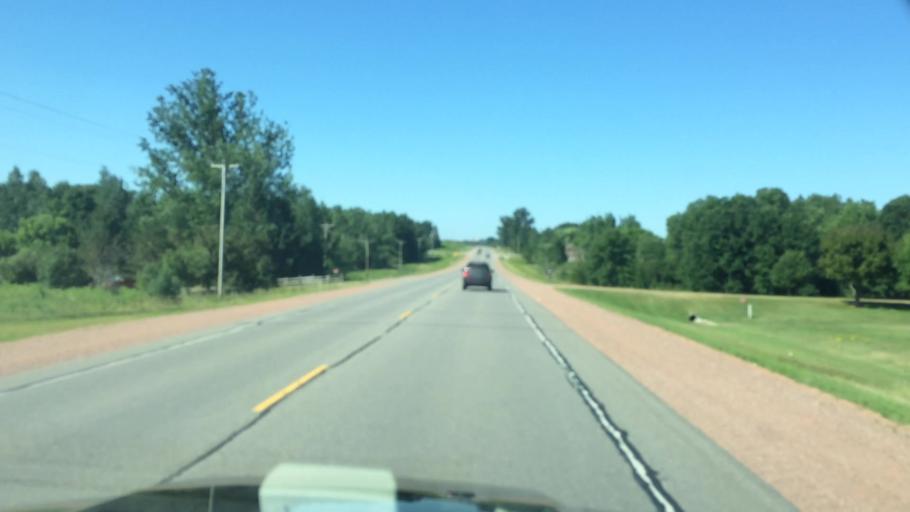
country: US
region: Wisconsin
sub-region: Wood County
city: Marshfield
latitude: 44.7132
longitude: -90.1154
